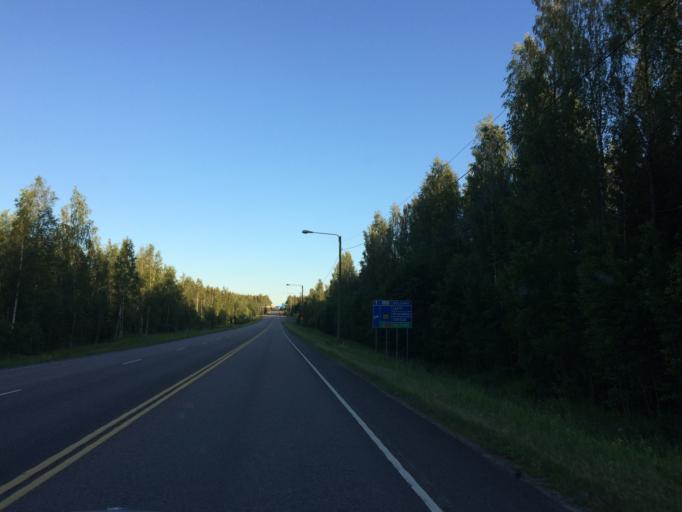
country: FI
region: Haeme
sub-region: Riihimaeki
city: Riihimaeki
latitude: 60.7548
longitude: 24.7207
